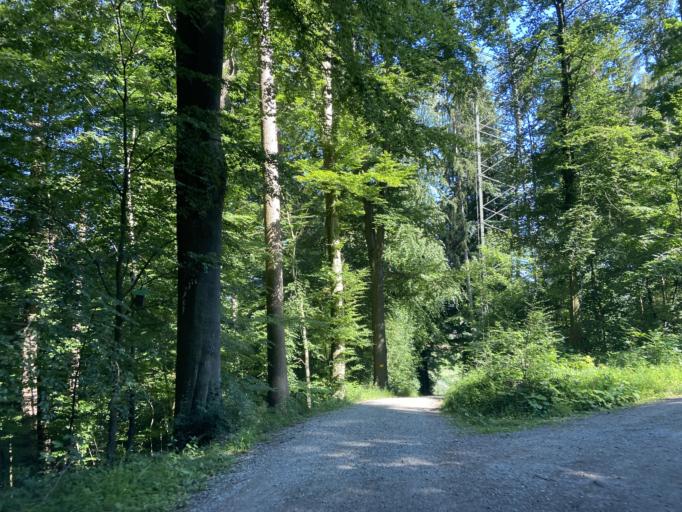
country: CH
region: Zurich
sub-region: Bezirk Winterthur
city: Wuelflingen (Kreis 6) / Niederfeld
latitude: 47.5033
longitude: 8.6682
